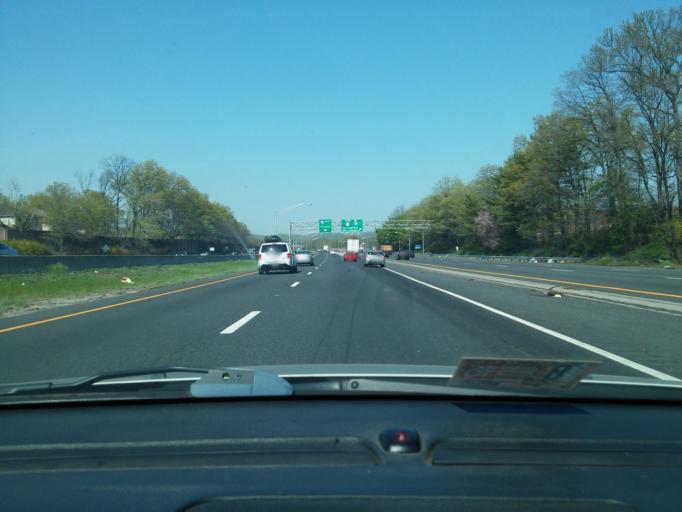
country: US
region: New Jersey
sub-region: Essex County
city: Maplewood
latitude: 40.7144
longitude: -74.2837
